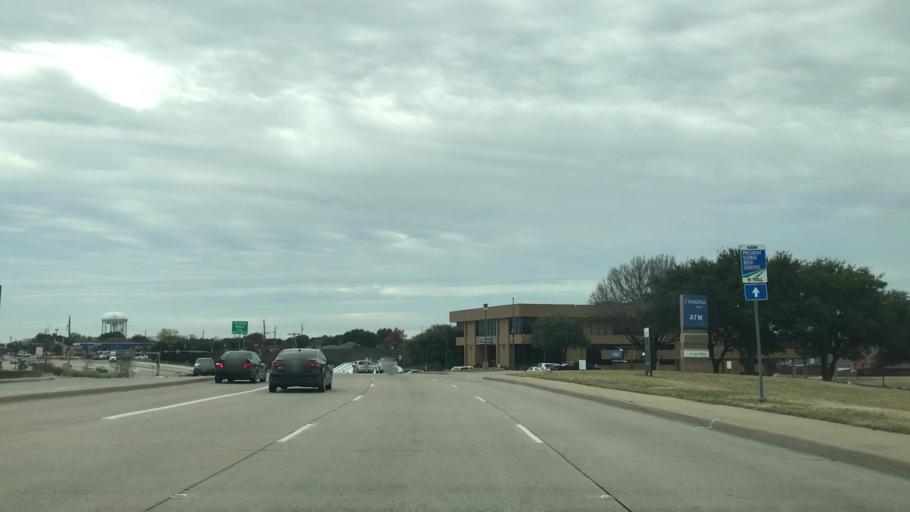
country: US
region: Texas
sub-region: Dallas County
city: Carrollton
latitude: 32.9882
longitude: -96.8906
